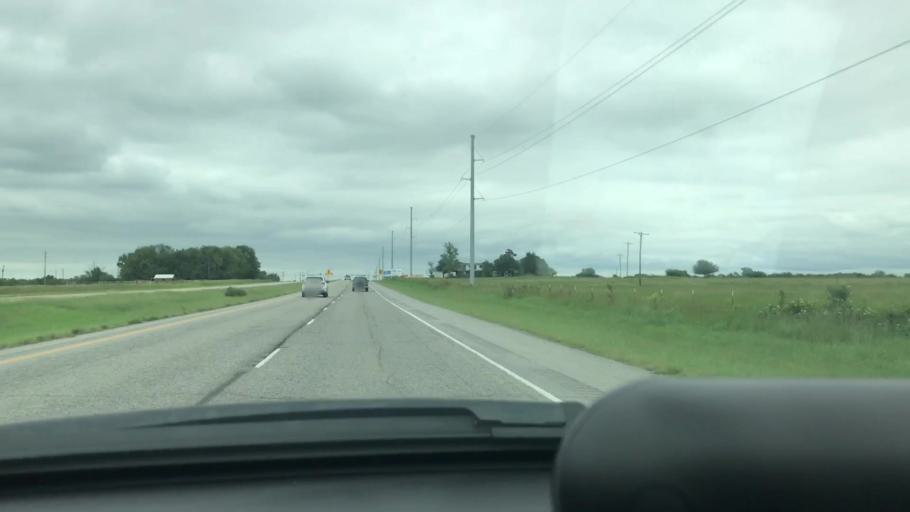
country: US
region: Oklahoma
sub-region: Wagoner County
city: Wagoner
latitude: 36.0120
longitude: -95.3686
